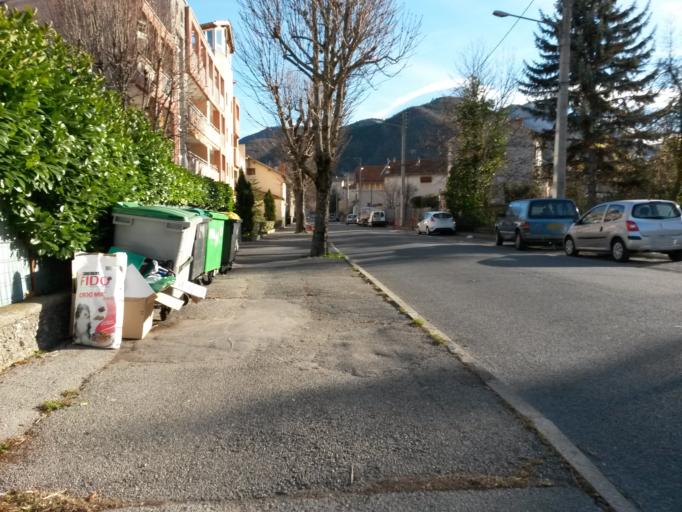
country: FR
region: Provence-Alpes-Cote d'Azur
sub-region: Departement des Alpes-de-Haute-Provence
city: Digne-les-Bains
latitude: 44.0987
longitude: 6.2328
